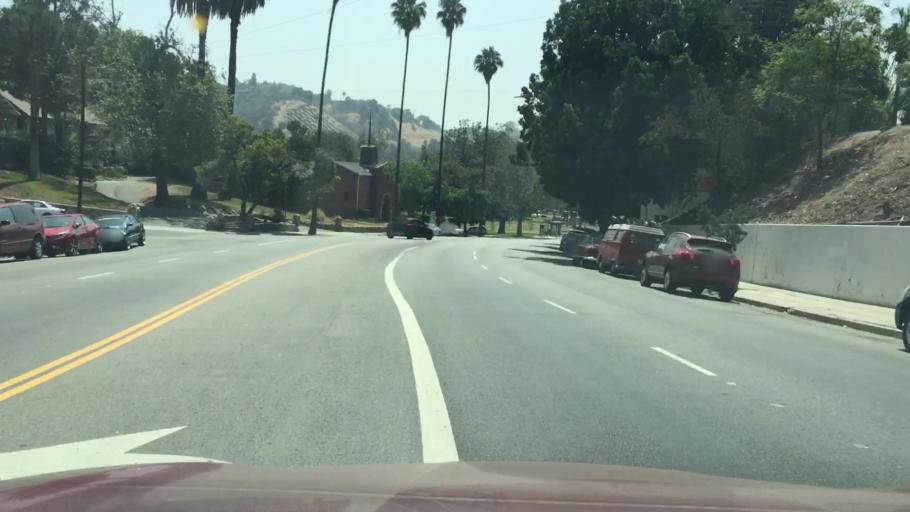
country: US
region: California
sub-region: Los Angeles County
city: South Pasadena
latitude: 34.1036
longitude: -118.2030
